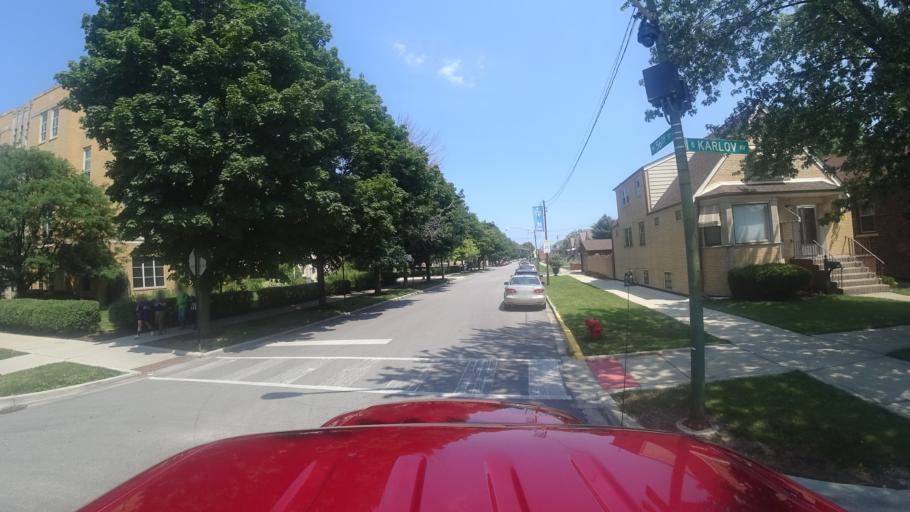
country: US
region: Illinois
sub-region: Cook County
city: Hometown
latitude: 41.7913
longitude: -87.7255
